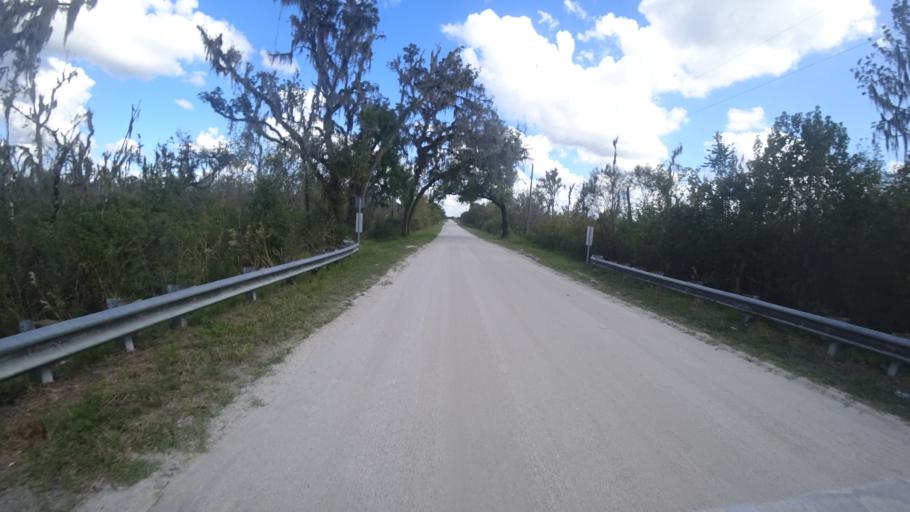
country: US
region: Florida
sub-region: Sarasota County
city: Lake Sarasota
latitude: 27.4230
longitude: -82.1410
